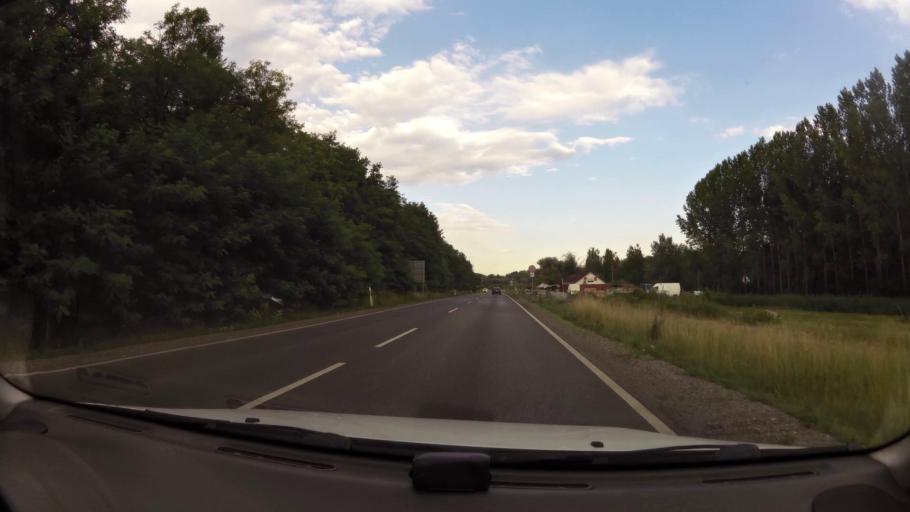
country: HU
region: Pest
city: Gyomro
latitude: 47.4282
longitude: 19.4265
